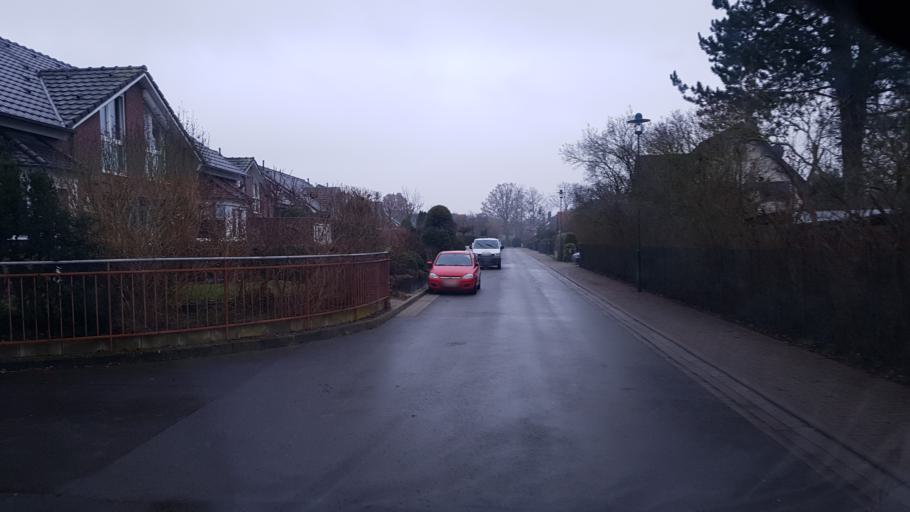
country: DE
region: Brandenburg
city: Stahnsdorf
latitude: 52.3749
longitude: 13.2175
